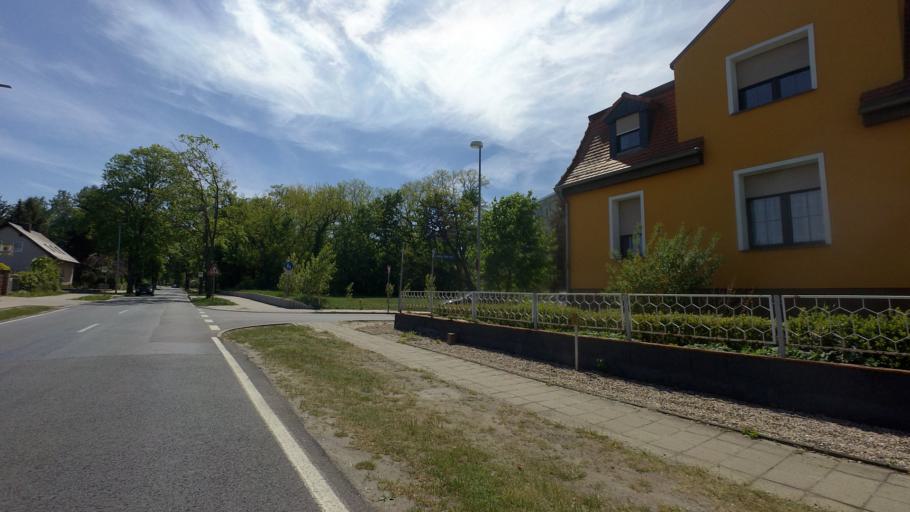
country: DE
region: Brandenburg
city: Luckenwalde
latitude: 52.1036
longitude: 13.1544
